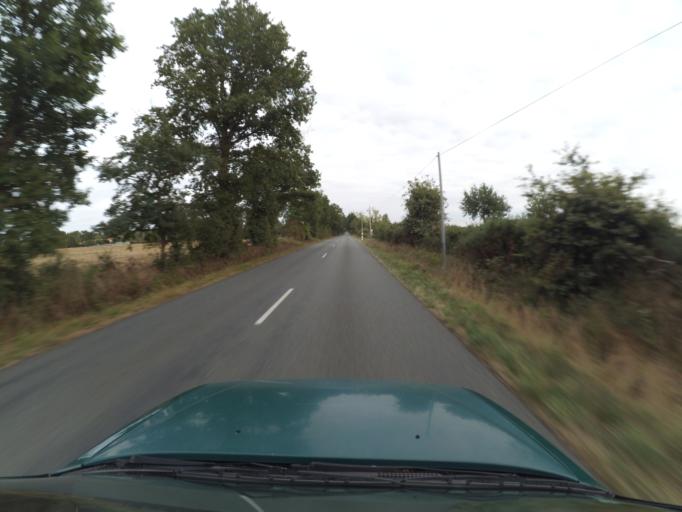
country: FR
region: Pays de la Loire
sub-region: Departement de la Loire-Atlantique
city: Montbert
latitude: 47.0286
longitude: -1.4977
